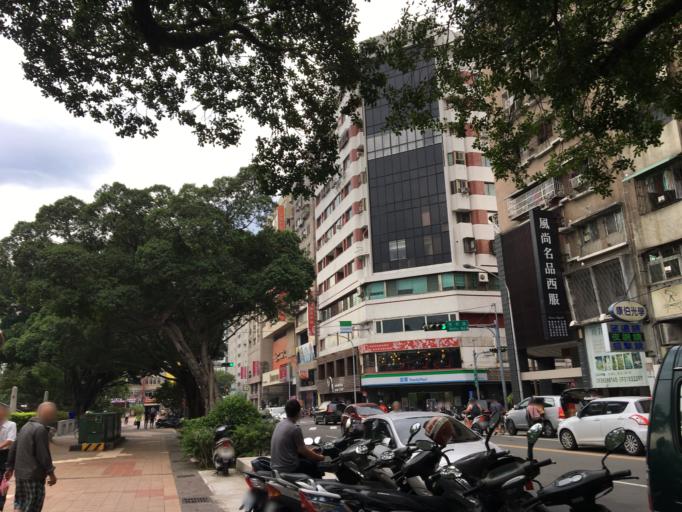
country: TW
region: Taiwan
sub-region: Taichung City
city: Taichung
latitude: 24.1433
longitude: 120.6833
